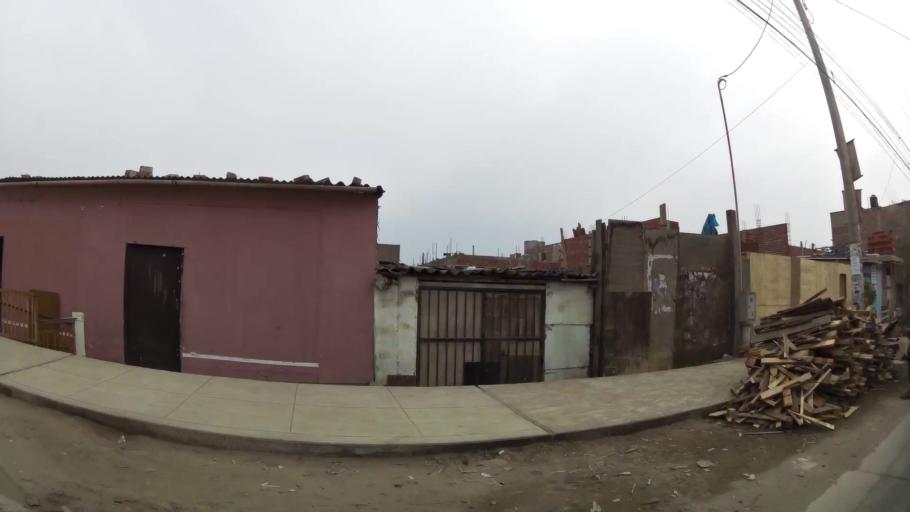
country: PE
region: Lima
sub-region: Lima
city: Surco
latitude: -12.2398
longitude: -76.9336
